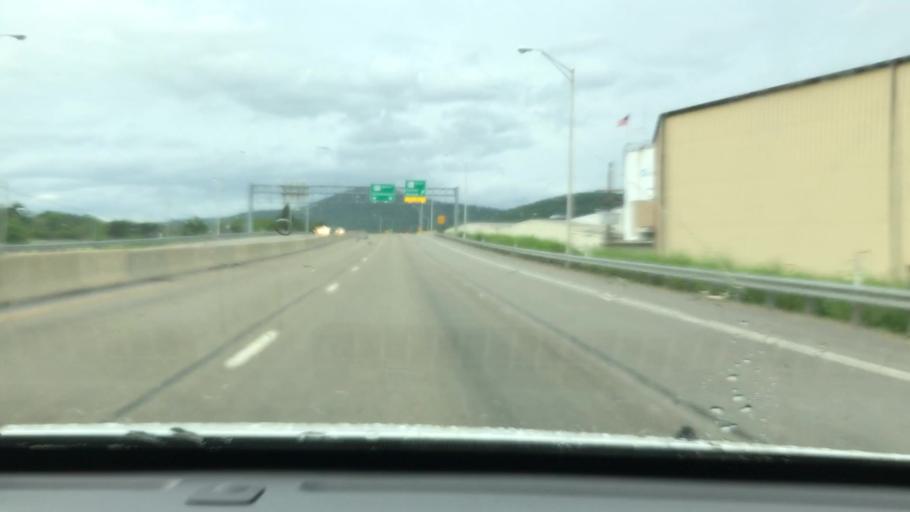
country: US
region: Pennsylvania
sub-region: McKean County
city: Foster Brook
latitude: 41.9743
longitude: -78.6269
